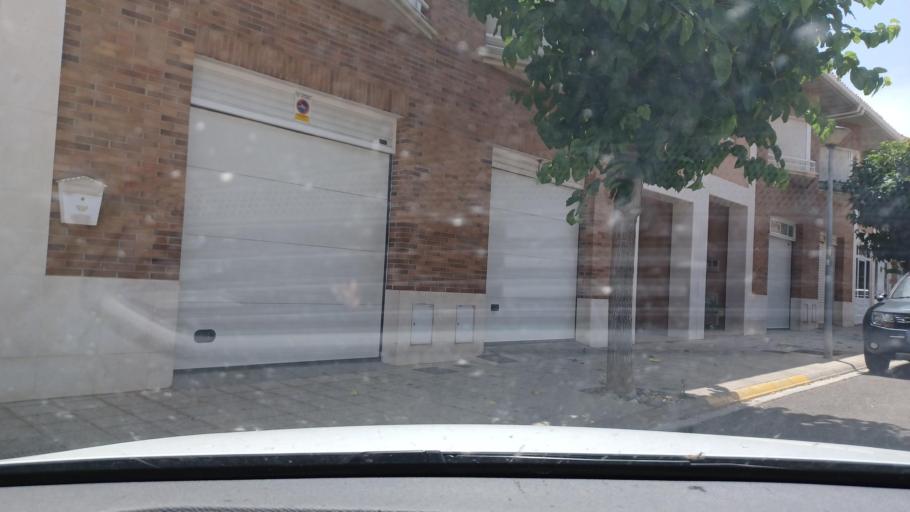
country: ES
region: Navarre
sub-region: Provincia de Navarra
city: Tudela
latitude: 42.0645
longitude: -1.6167
